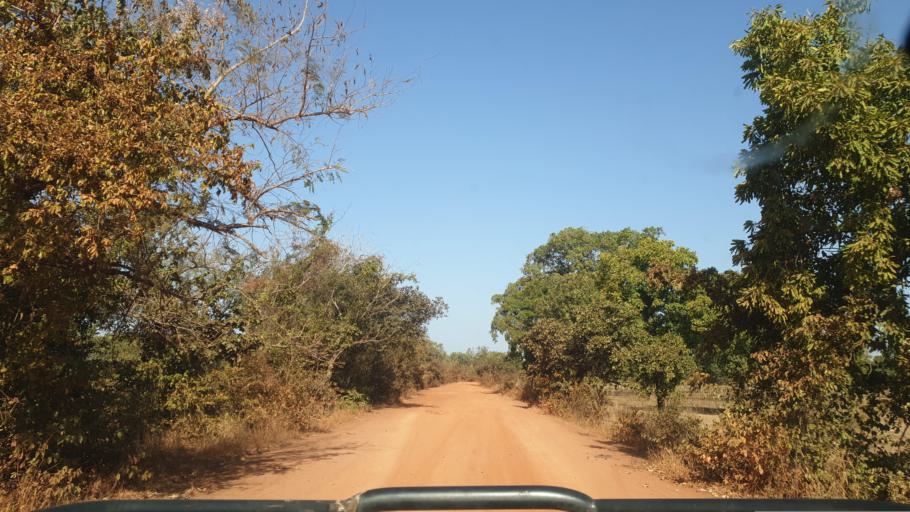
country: ML
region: Sikasso
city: Bougouni
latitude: 11.7751
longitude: -6.9051
